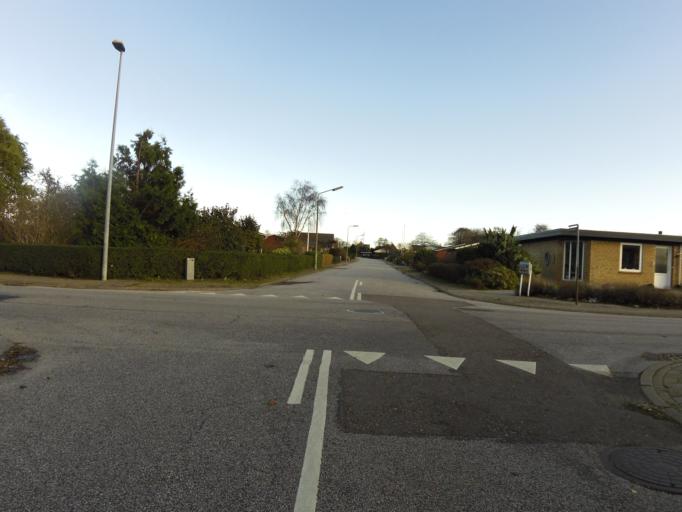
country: DK
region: South Denmark
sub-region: Tonder Kommune
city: Sherrebek
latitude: 55.1542
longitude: 8.7665
